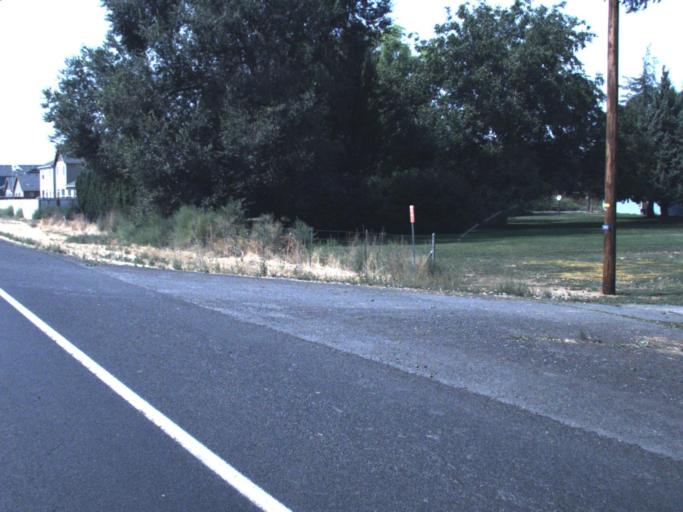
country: US
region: Washington
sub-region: Yakima County
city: Terrace Heights
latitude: 46.5494
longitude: -120.3677
